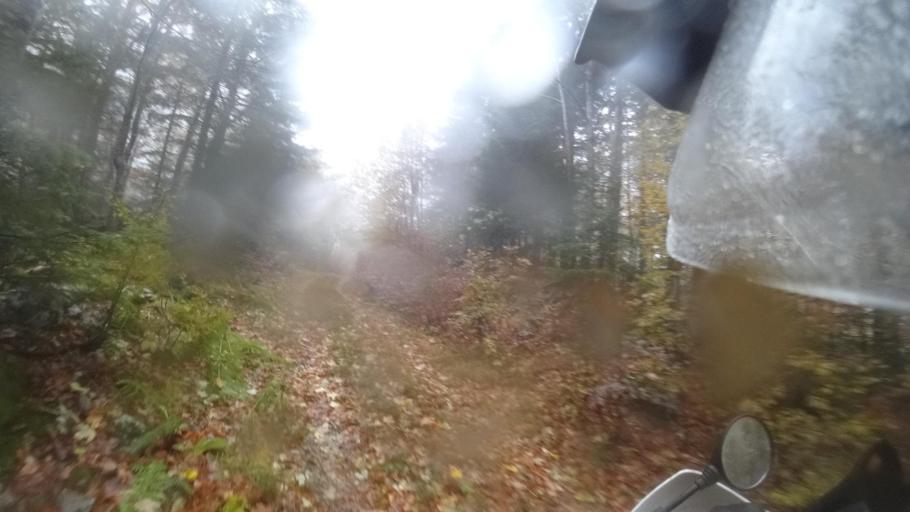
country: HR
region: Primorsko-Goranska
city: Vrbovsko
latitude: 45.2823
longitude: 14.9673
